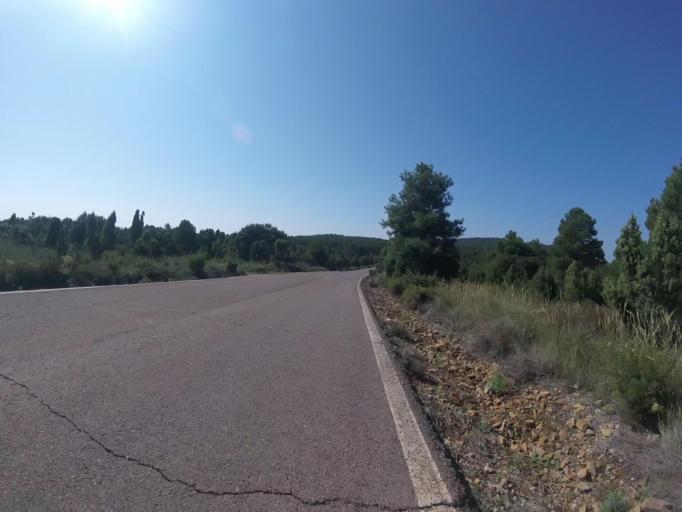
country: ES
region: Valencia
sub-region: Provincia de Castello
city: Benafigos
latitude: 40.2862
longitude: -0.2383
